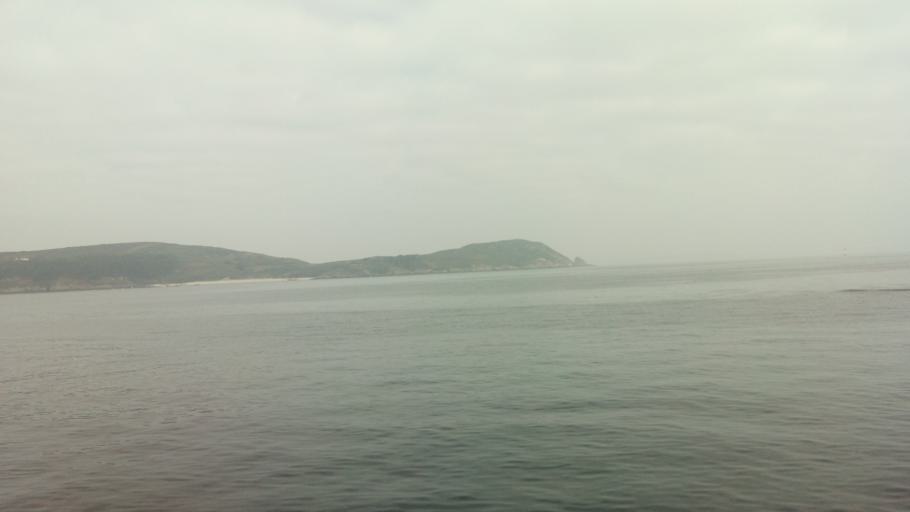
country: ES
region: Galicia
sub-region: Provincia de Pontevedra
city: Sanxenxo
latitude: 42.3789
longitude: -8.9135
